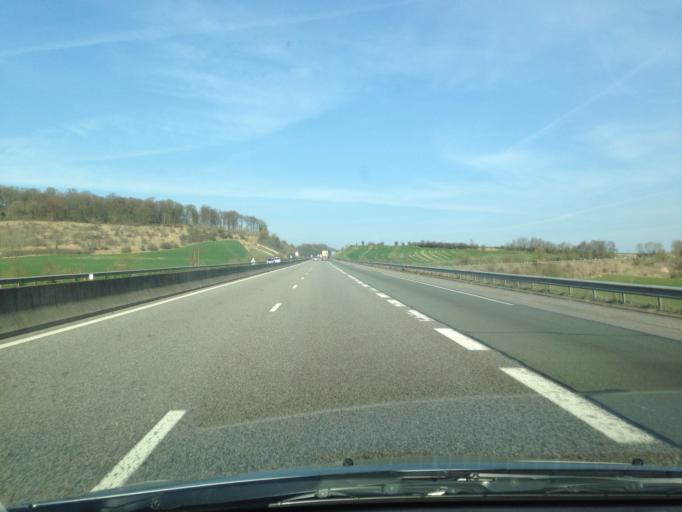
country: FR
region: Haute-Normandie
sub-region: Departement de la Seine-Maritime
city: Neufchatel-en-Bray
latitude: 49.7279
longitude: 1.4560
